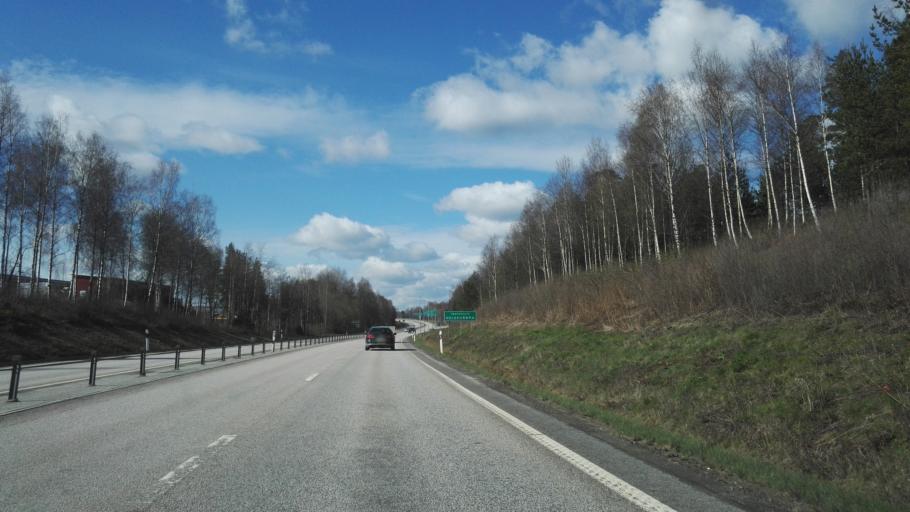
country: SE
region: Kronoberg
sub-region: Vaxjo Kommun
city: Vaexjoe
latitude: 56.8925
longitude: 14.7658
